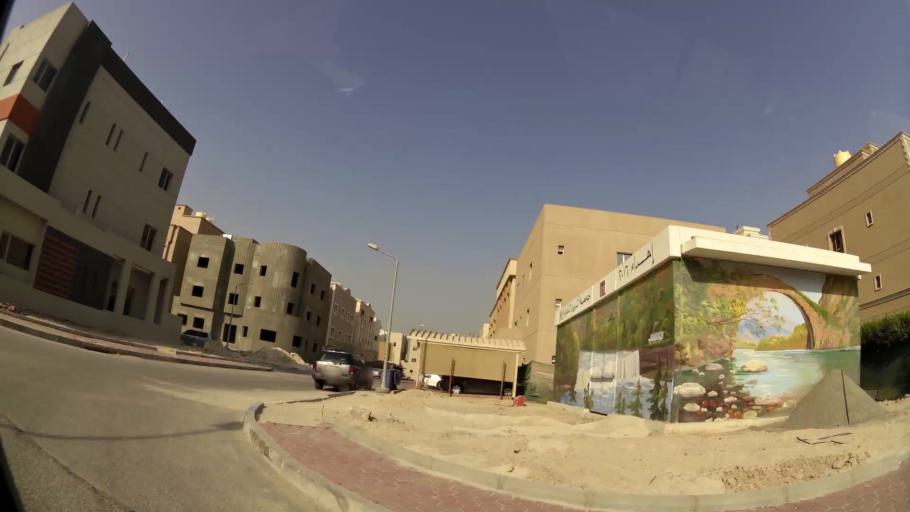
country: KW
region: Al Asimah
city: Ar Rabiyah
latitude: 29.3004
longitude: 47.8096
